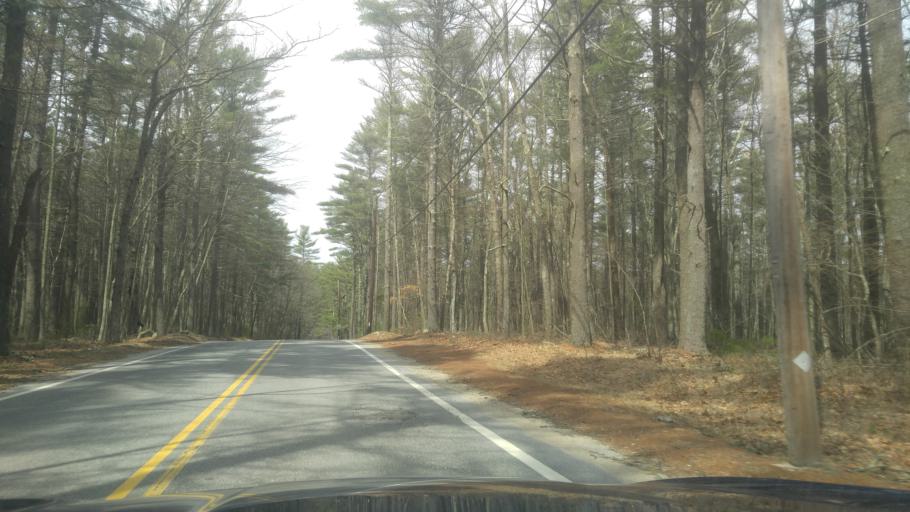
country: US
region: Rhode Island
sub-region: Washington County
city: Exeter
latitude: 41.6341
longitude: -71.5729
